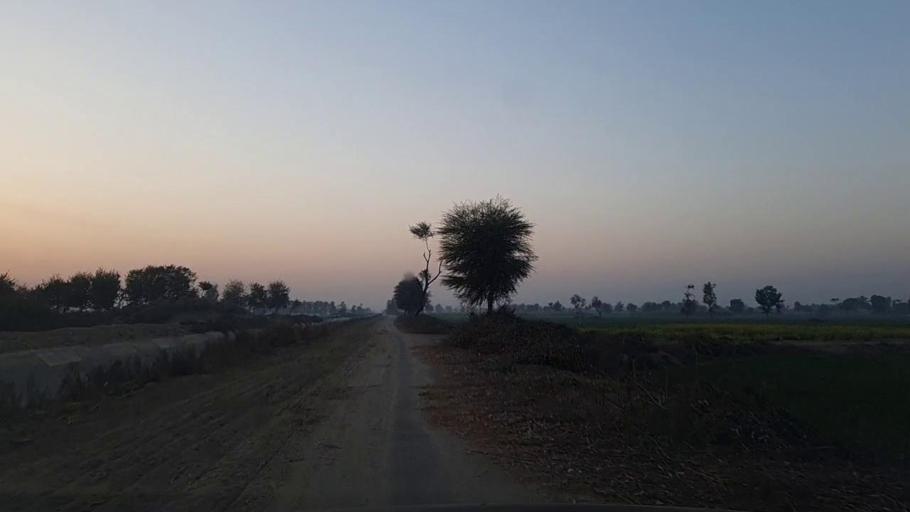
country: PK
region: Sindh
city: Daur
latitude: 26.4773
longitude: 68.4968
